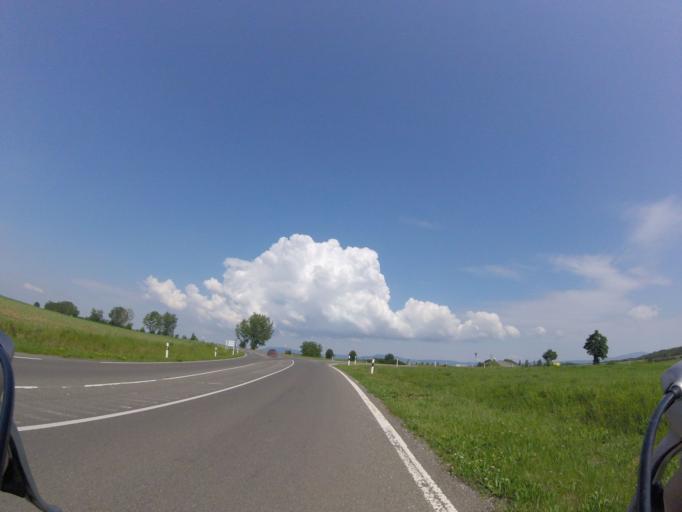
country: HU
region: Baranya
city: Kozarmisleny
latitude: 46.0163
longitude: 18.3040
